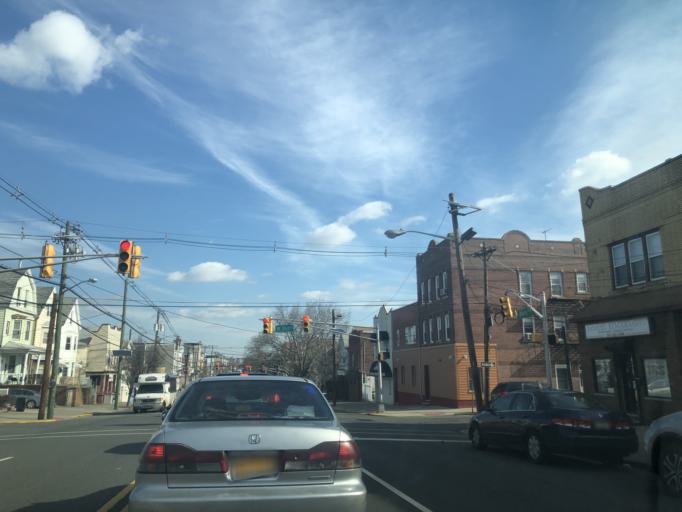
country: US
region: New Jersey
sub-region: Hudson County
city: Bayonne
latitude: 40.6646
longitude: -74.1242
